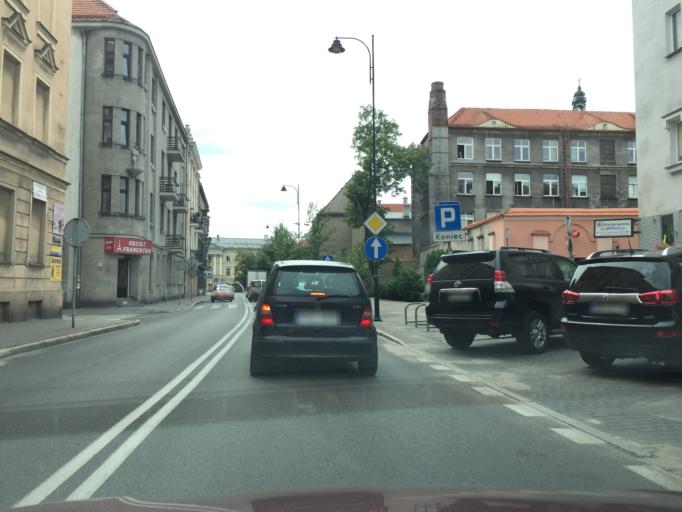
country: PL
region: Greater Poland Voivodeship
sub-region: Kalisz
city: Kalisz
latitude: 51.7617
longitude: 18.0907
